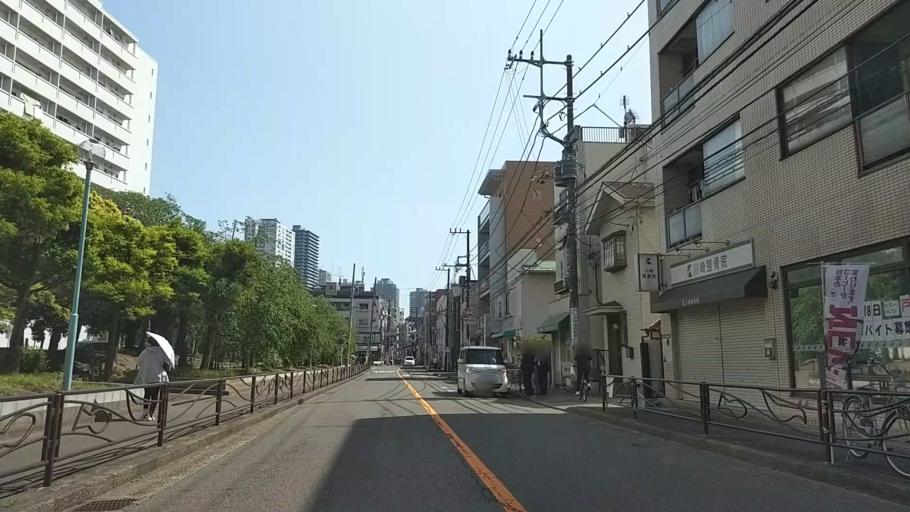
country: JP
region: Kanagawa
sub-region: Kawasaki-shi
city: Kawasaki
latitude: 35.5394
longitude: 139.6914
